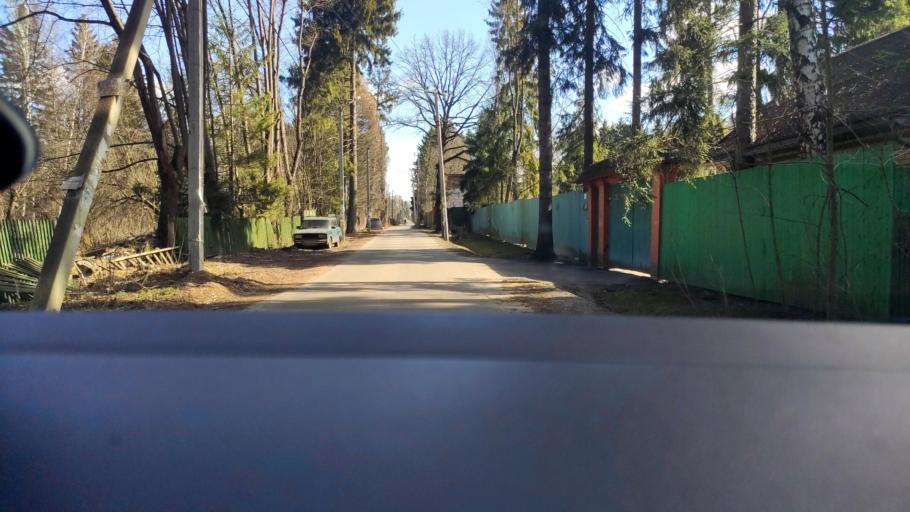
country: RU
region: Moskovskaya
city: Aprelevka
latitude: 55.5409
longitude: 37.0441
